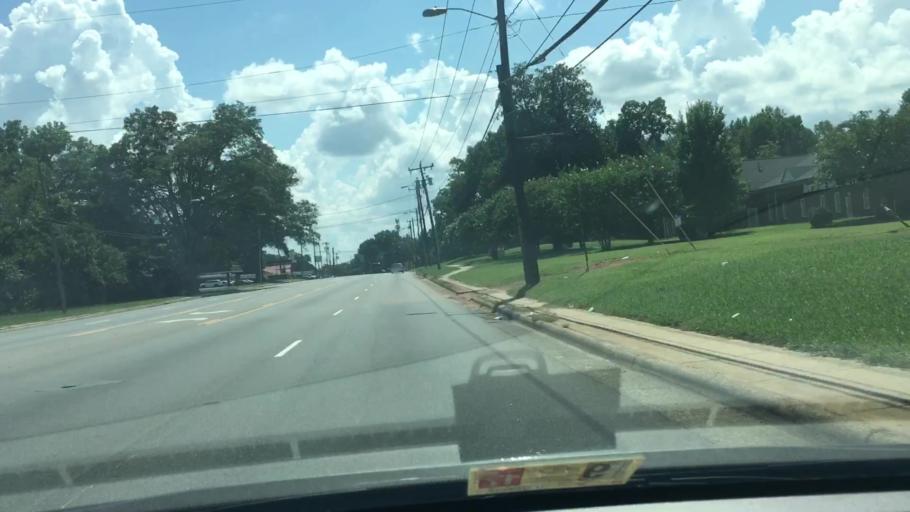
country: US
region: North Carolina
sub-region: Mecklenburg County
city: Charlotte
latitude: 35.2699
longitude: -80.7944
